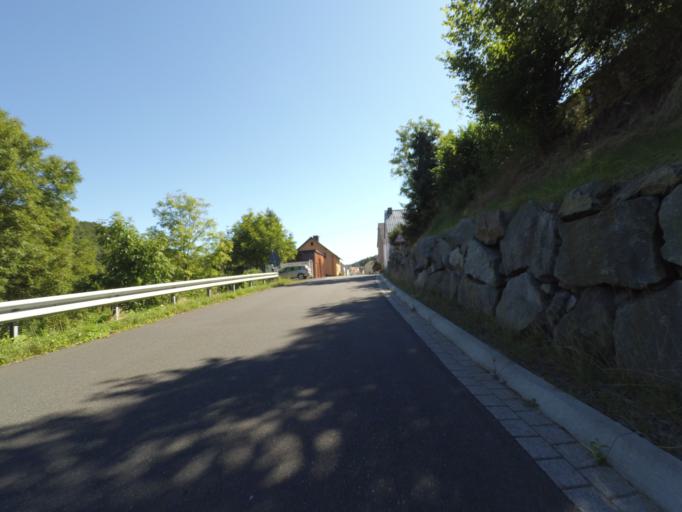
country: DE
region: Rheinland-Pfalz
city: Immerath
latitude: 50.1474
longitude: 6.9534
